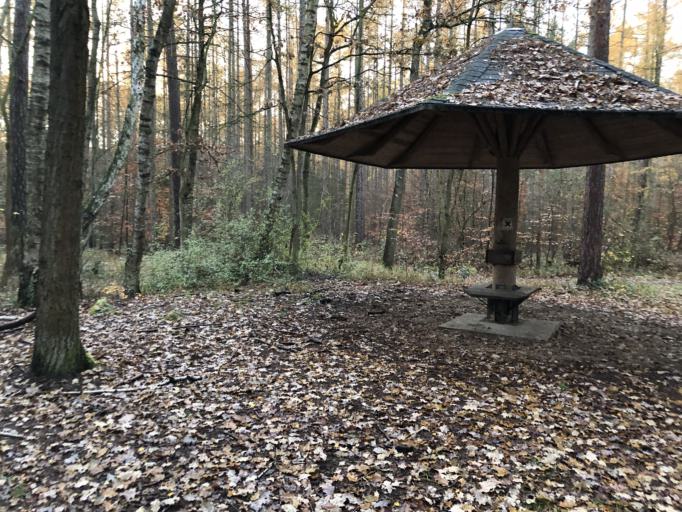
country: DE
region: Saxony-Anhalt
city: Lieskau
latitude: 51.4967
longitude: 11.8807
